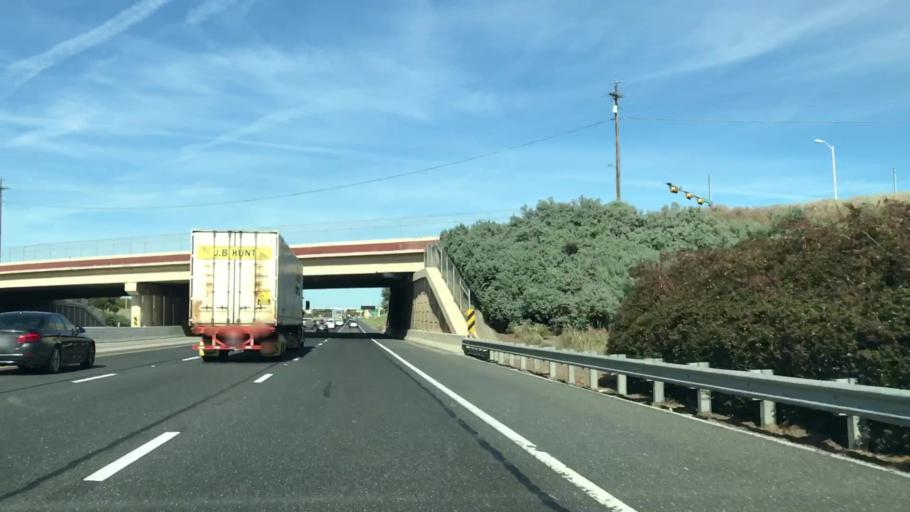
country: US
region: Texas
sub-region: Dallas County
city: Addison
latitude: 33.0005
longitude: -96.8568
